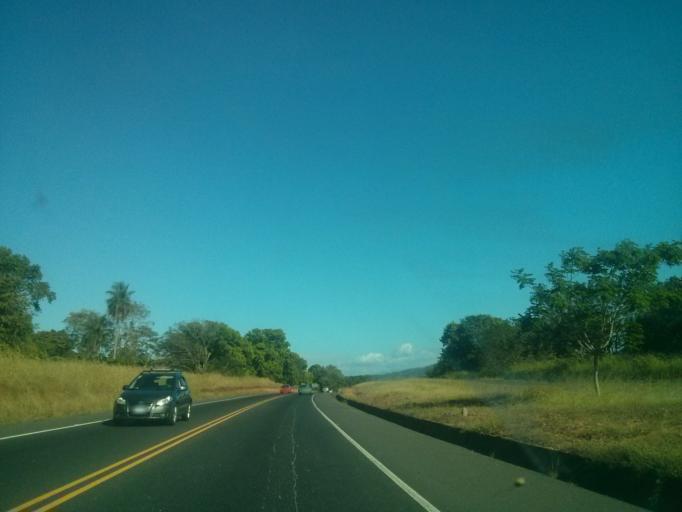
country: CR
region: Alajuela
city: Orotina
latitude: 9.9186
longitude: -84.4972
